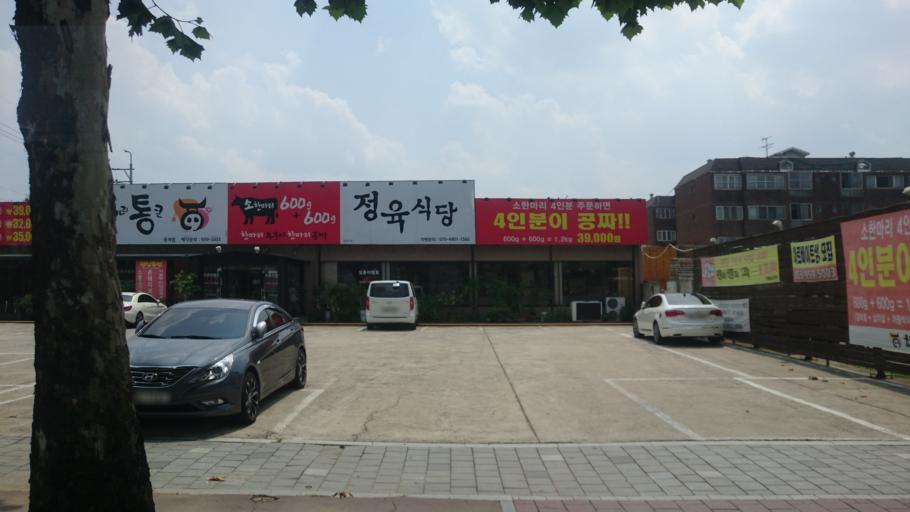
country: KR
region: Gyeongsangbuk-do
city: Gyeongsan-si
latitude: 35.8768
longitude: 128.6796
